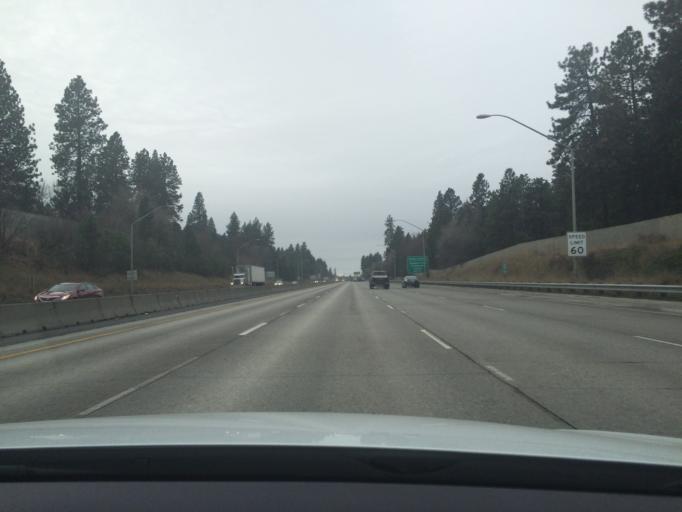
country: US
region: Washington
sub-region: Spokane County
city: Spokane
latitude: 47.6443
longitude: -117.4575
